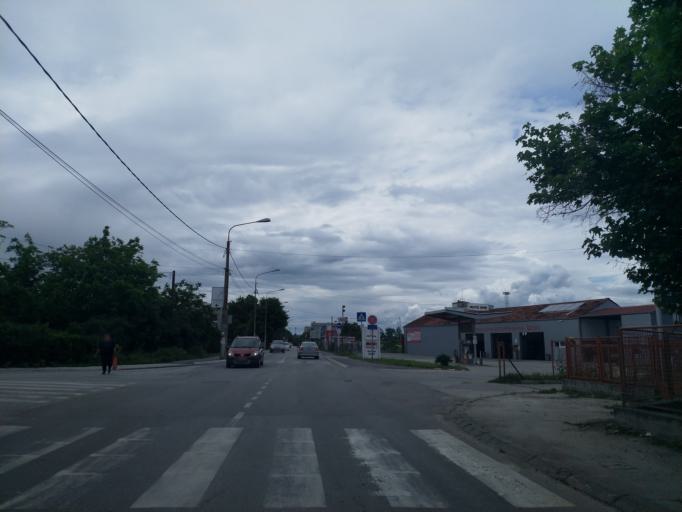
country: RS
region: Central Serbia
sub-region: Pomoravski Okrug
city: Jagodina
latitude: 43.9766
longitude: 21.2706
